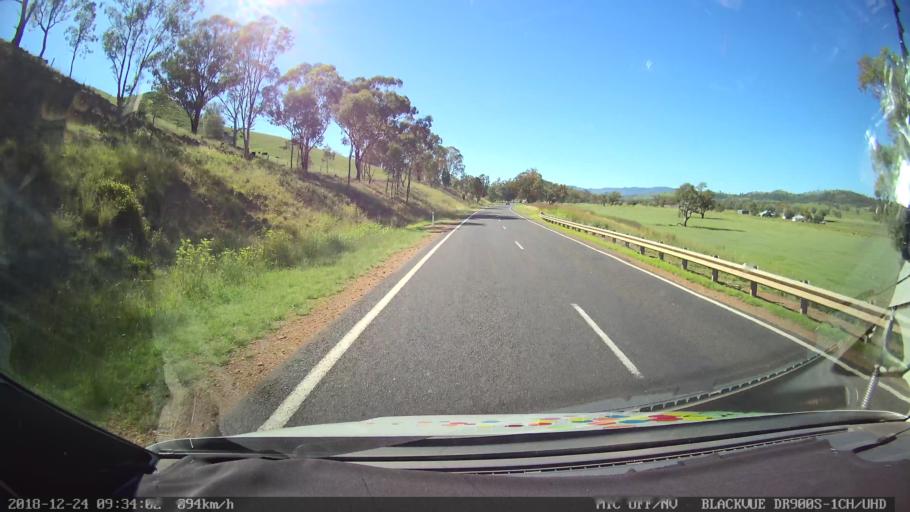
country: AU
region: New South Wales
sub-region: Liverpool Plains
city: Quirindi
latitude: -31.6097
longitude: 150.7132
